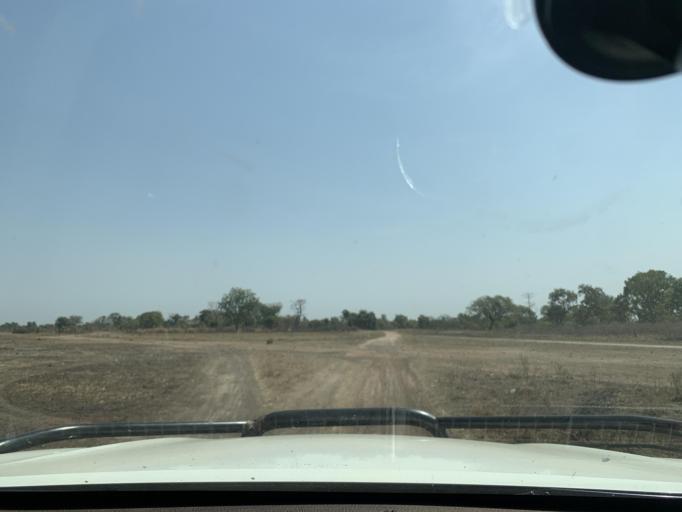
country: ML
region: Sikasso
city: Kolondieba
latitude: 10.8411
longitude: -6.8024
